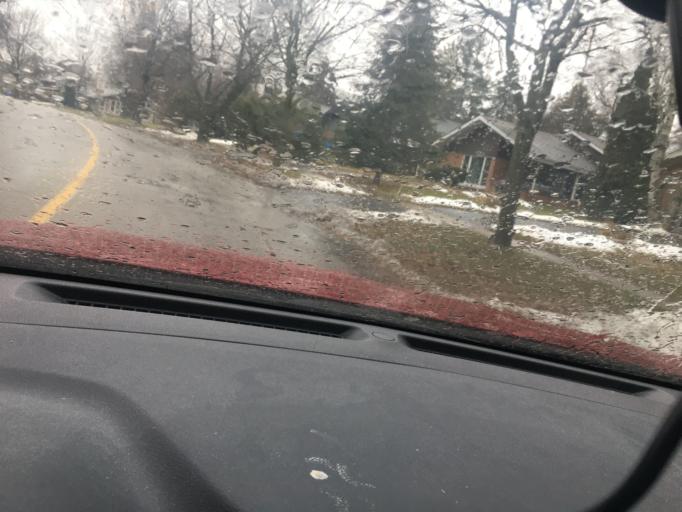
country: CA
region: Ontario
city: Scarborough
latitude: 43.7643
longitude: -79.2673
